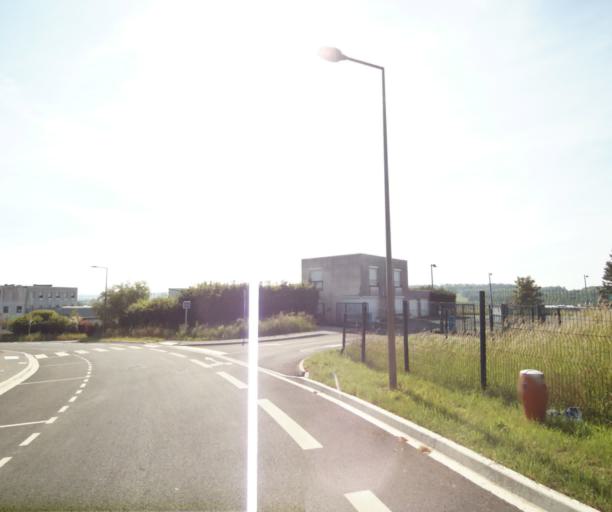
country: FR
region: Champagne-Ardenne
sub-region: Departement des Ardennes
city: La Francheville
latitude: 49.7381
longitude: 4.7190
